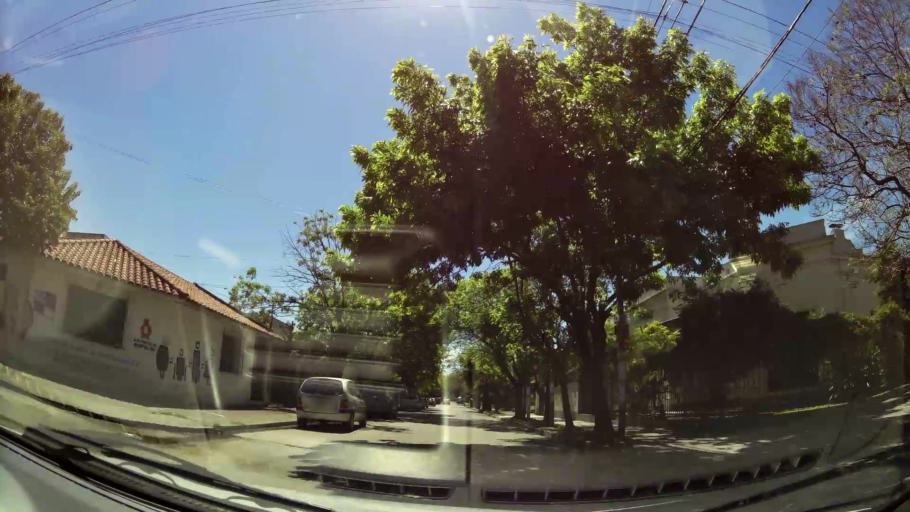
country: AR
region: Buenos Aires
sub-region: Partido de Quilmes
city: Quilmes
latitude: -34.7218
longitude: -58.2484
